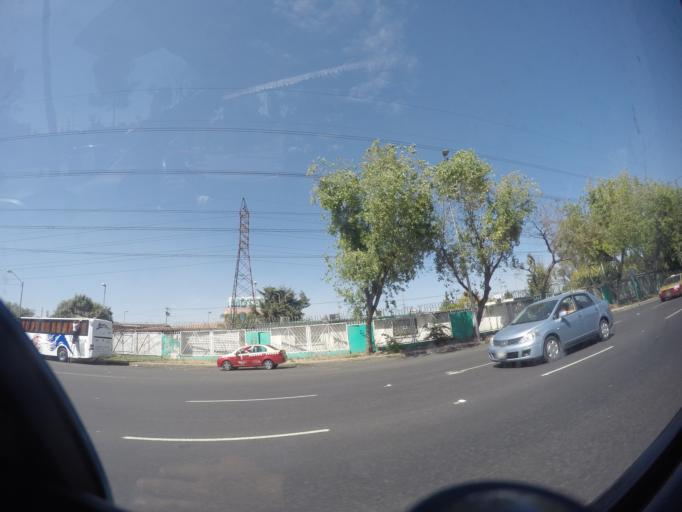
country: MX
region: Mexico
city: Colonia Lindavista
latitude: 19.4734
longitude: -99.1353
